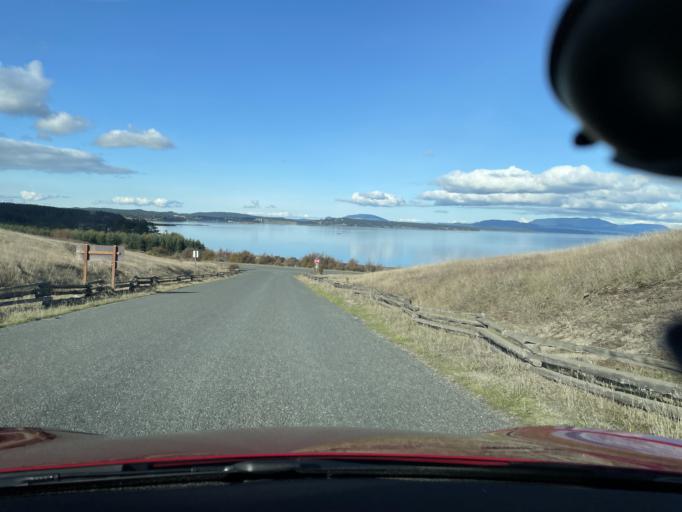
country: US
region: Washington
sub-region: San Juan County
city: Friday Harbor
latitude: 48.4629
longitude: -123.0015
